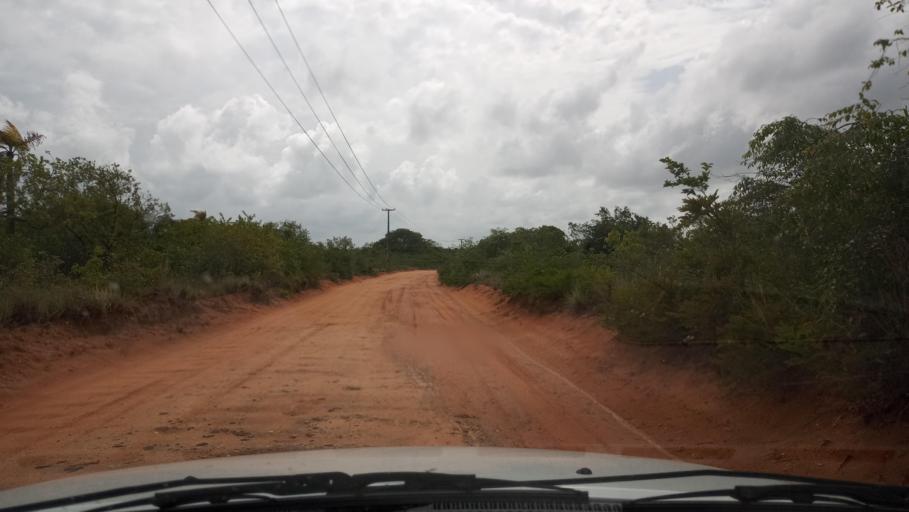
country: BR
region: Rio Grande do Norte
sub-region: Maxaranguape
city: Sao Miguel
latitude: -5.4831
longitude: -35.3204
